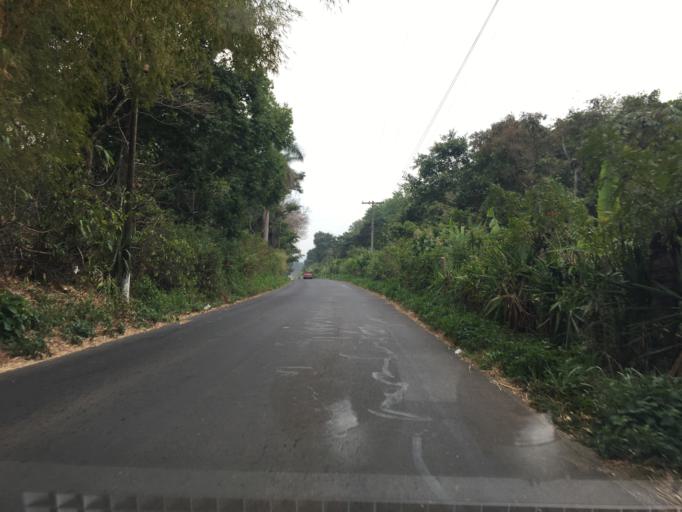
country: GT
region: Guatemala
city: Fraijanes
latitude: 14.3958
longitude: -90.4735
